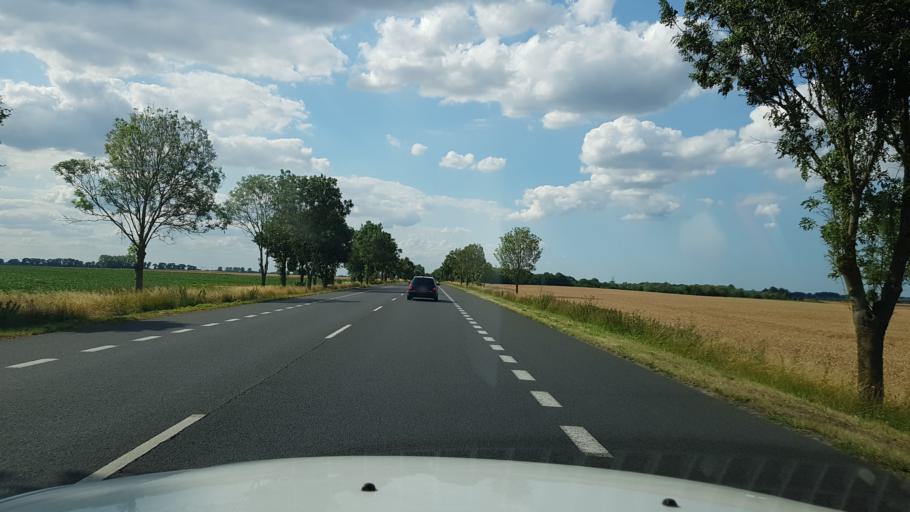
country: PL
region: West Pomeranian Voivodeship
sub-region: Powiat pyrzycki
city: Pyrzyce
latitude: 53.1608
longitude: 14.8700
